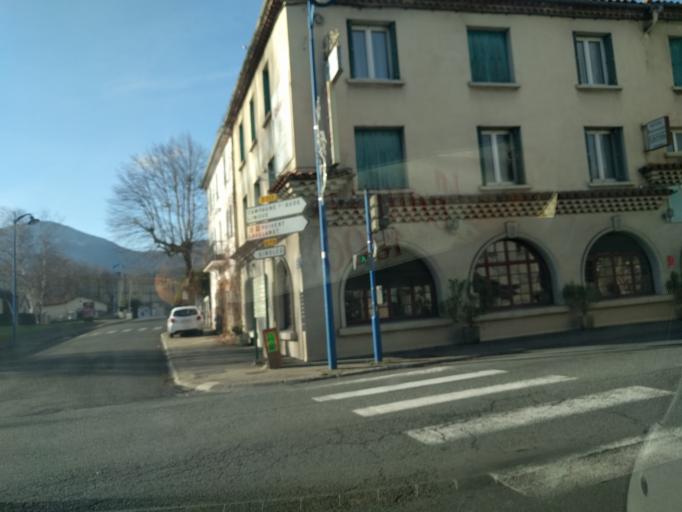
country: FR
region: Languedoc-Roussillon
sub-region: Departement de l'Aude
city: Quillan
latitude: 42.8756
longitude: 2.1825
